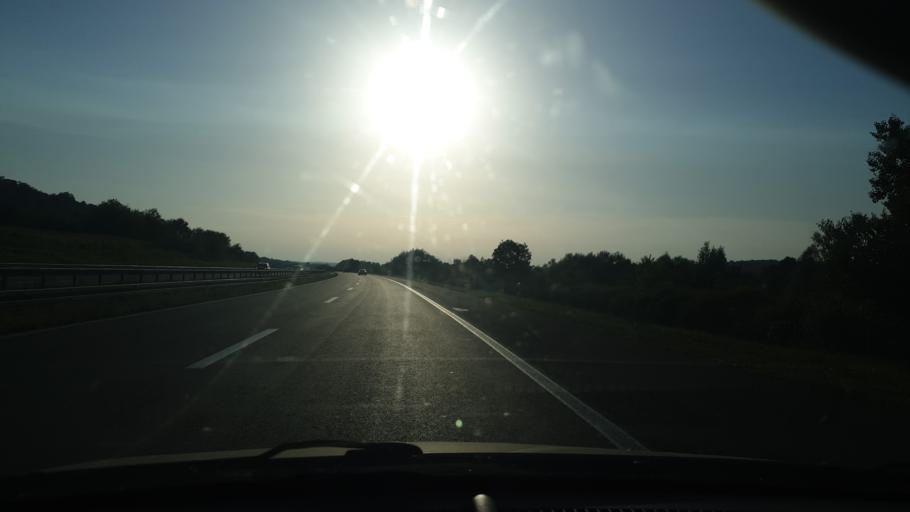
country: RS
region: Central Serbia
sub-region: Belgrade
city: Grocka
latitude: 44.5803
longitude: 20.7810
